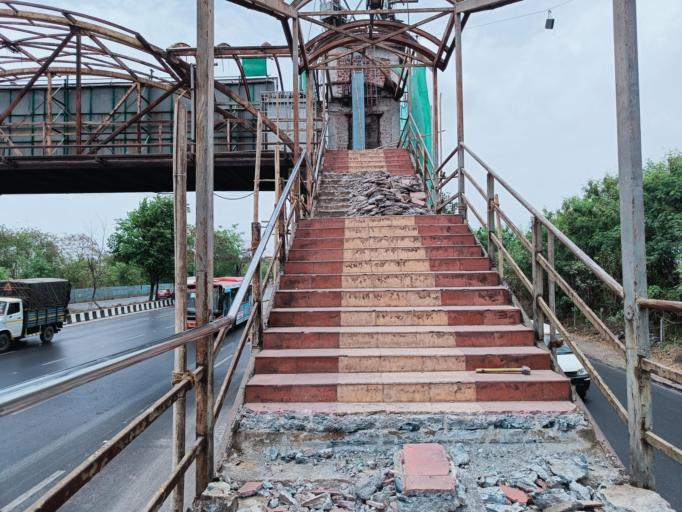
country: IN
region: Maharashtra
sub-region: Mumbai Suburban
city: Powai
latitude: 19.1312
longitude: 72.9413
